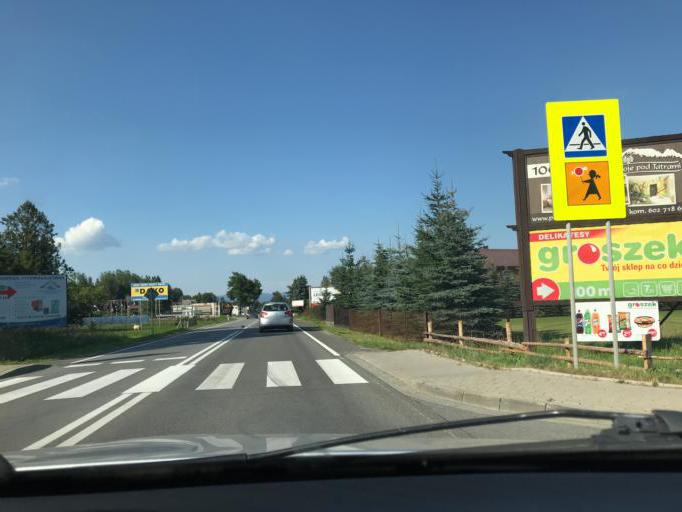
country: PL
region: Lesser Poland Voivodeship
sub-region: Powiat tatrzanski
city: Bialy Dunajec
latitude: 49.3748
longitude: 20.0074
